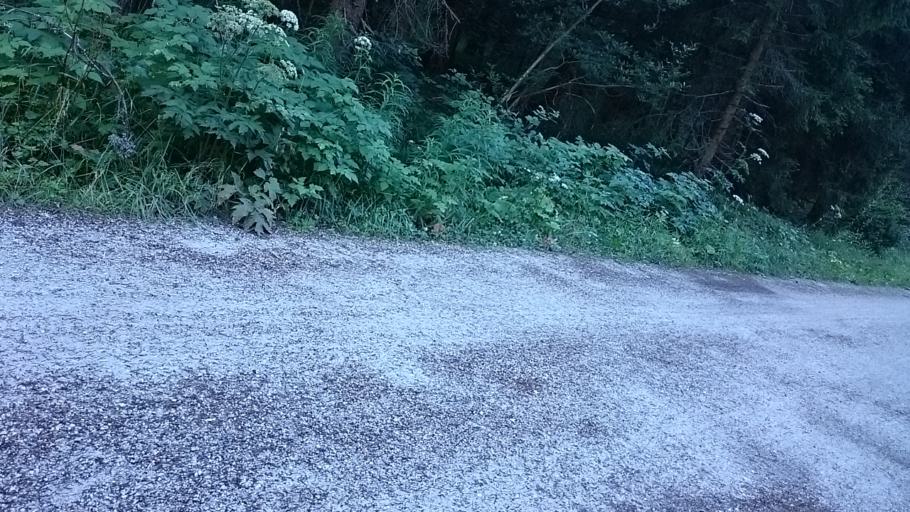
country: IT
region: Trentino-Alto Adige
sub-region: Bolzano
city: Dobbiaco
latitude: 46.7039
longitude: 12.2204
